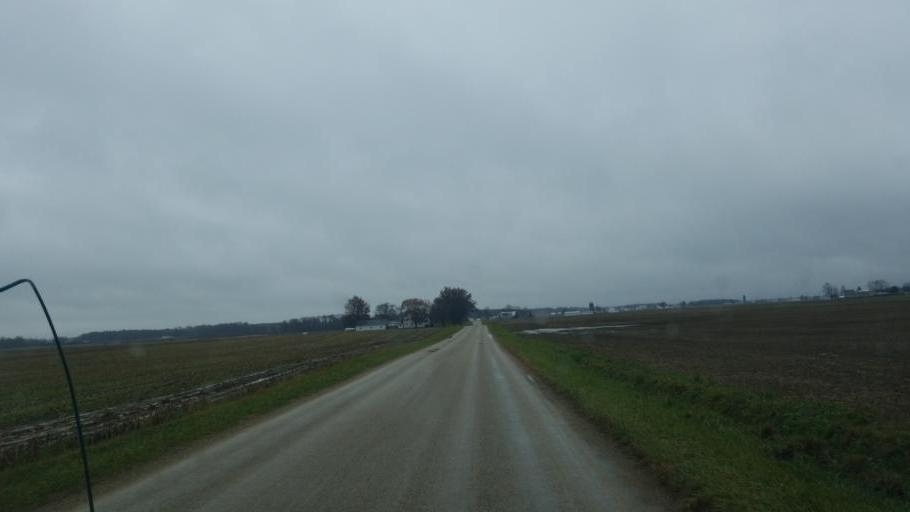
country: US
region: Indiana
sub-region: Adams County
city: Berne
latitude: 40.6648
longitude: -84.9173
